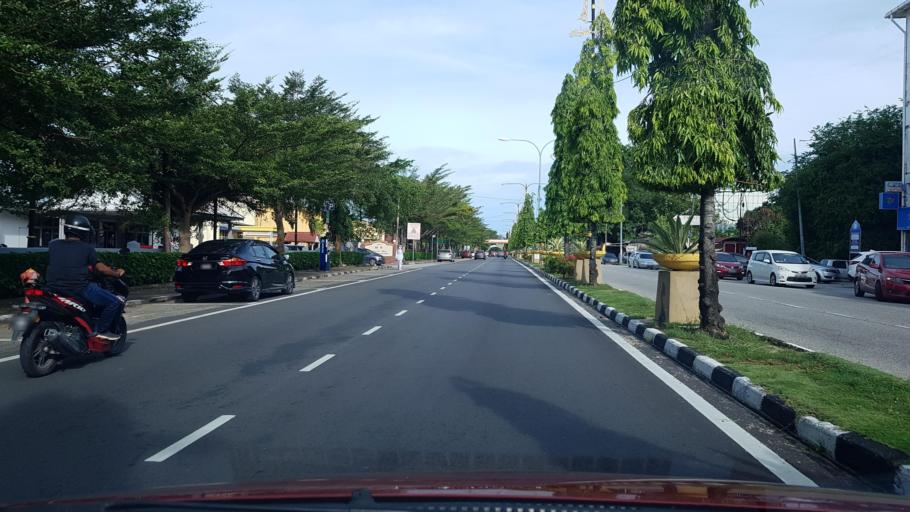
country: MY
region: Terengganu
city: Kuala Terengganu
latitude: 5.3266
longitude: 103.1480
